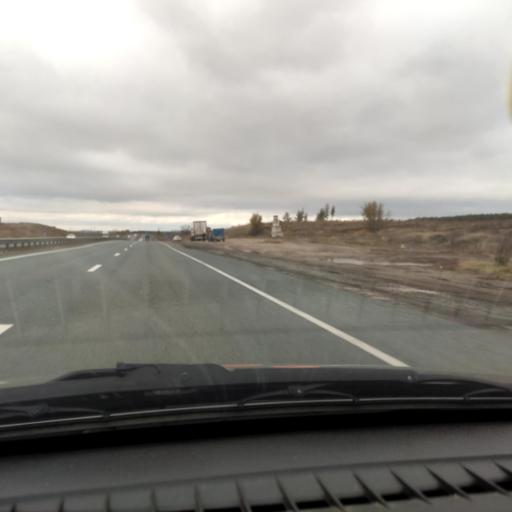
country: RU
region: Samara
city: Zhigulevsk
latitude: 53.5058
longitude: 49.5385
